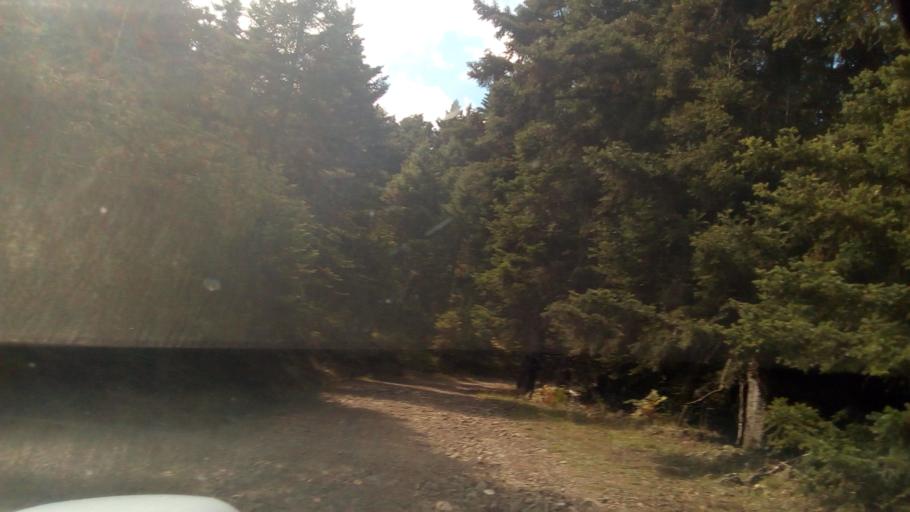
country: GR
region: Central Greece
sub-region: Nomos Fokidos
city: Lidoriki
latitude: 38.6411
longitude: 21.9523
